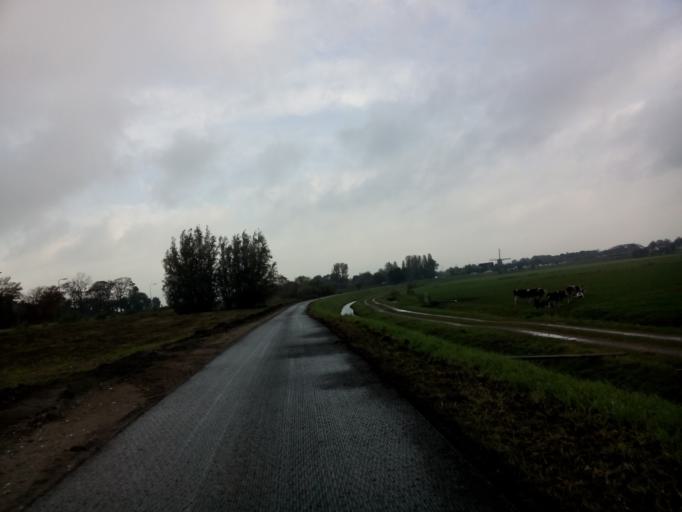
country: NL
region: South Holland
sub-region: Gemeente Westland
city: De Lier
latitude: 51.9677
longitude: 4.3044
